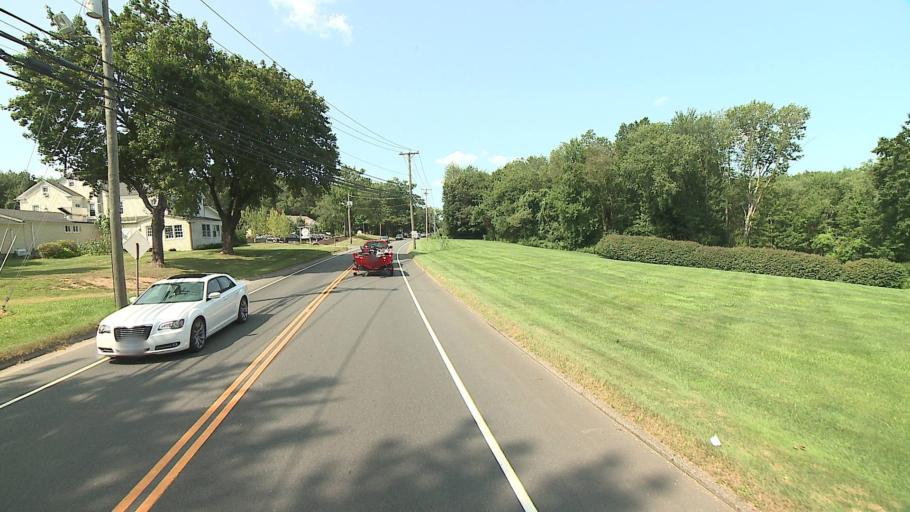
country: US
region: Connecticut
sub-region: Fairfield County
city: Newtown
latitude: 41.3825
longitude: -73.2844
